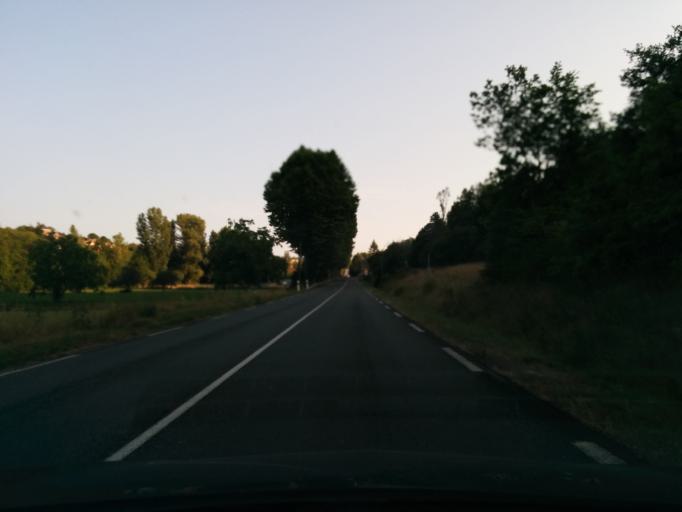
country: FR
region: Midi-Pyrenees
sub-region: Departement du Lot
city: Le Vigan
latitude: 44.6667
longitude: 1.4811
